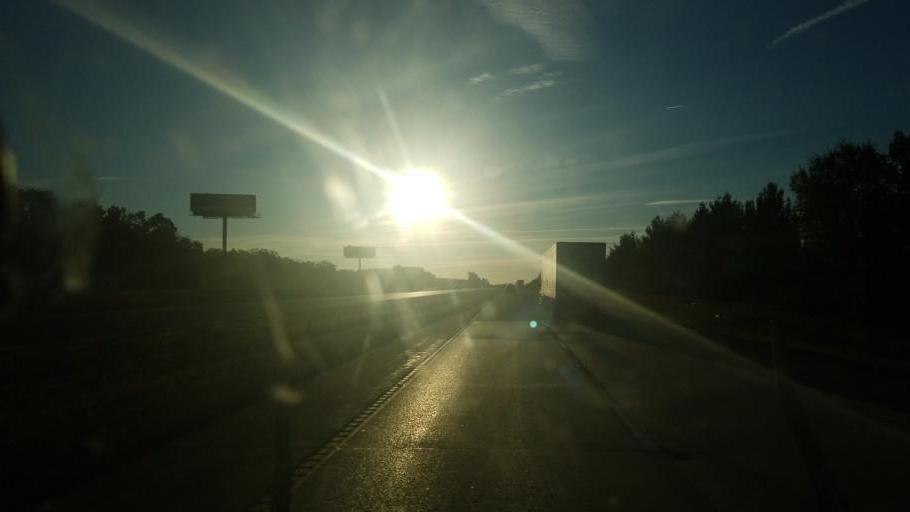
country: US
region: Missouri
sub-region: Montgomery County
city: Montgomery City
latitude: 38.9018
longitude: -91.6406
